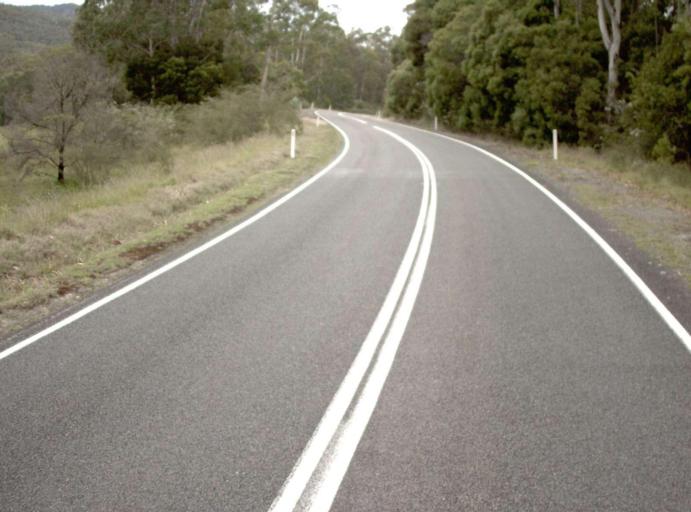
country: AU
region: New South Wales
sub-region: Bombala
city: Bombala
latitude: -37.2847
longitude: 149.2219
